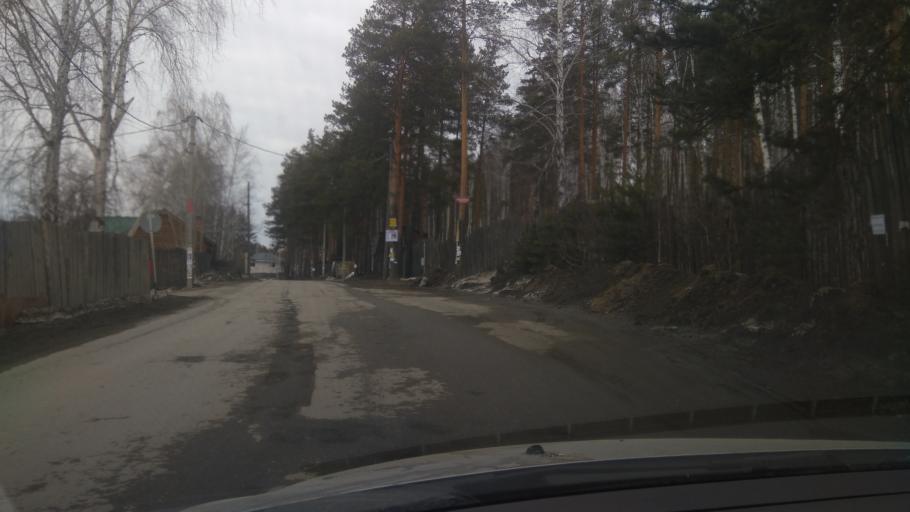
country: RU
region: Sverdlovsk
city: Severka
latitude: 56.8514
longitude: 60.3858
